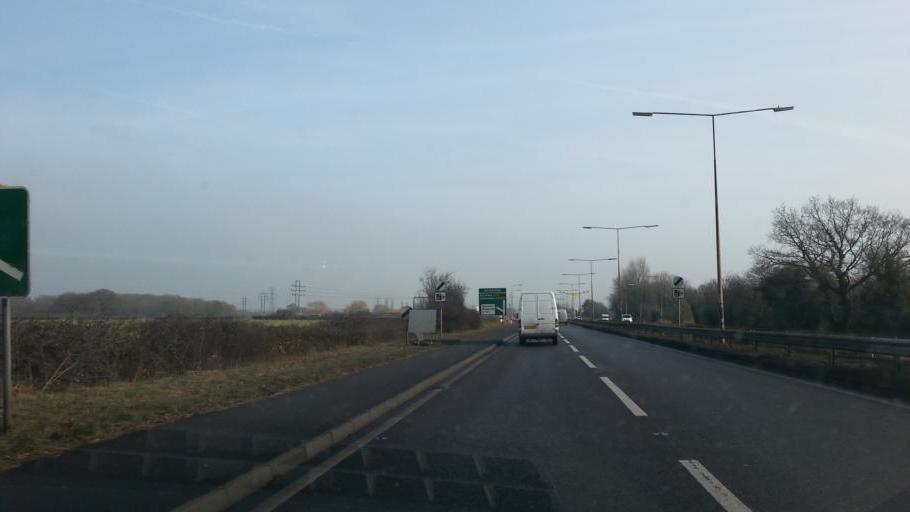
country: GB
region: England
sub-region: Essex
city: Pitsea
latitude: 51.5925
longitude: 0.4886
